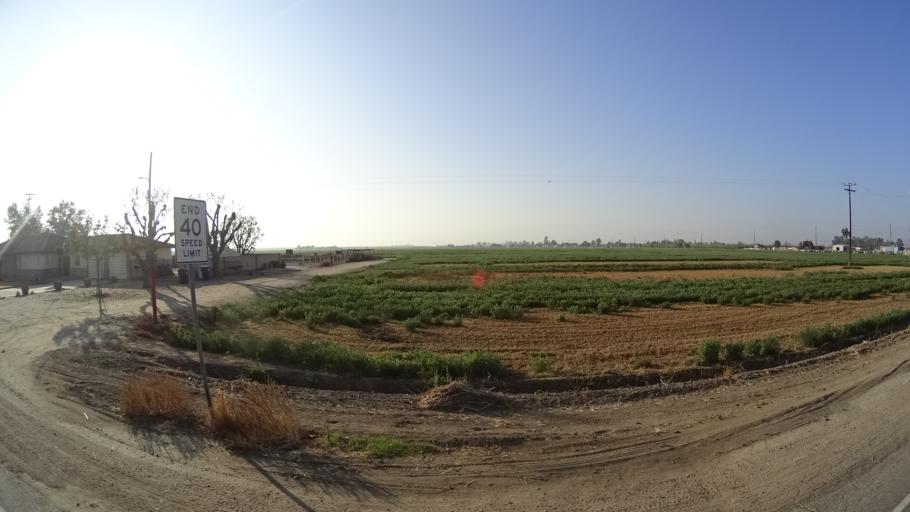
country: US
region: California
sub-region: Kern County
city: Greenfield
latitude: 35.2667
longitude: -118.9990
